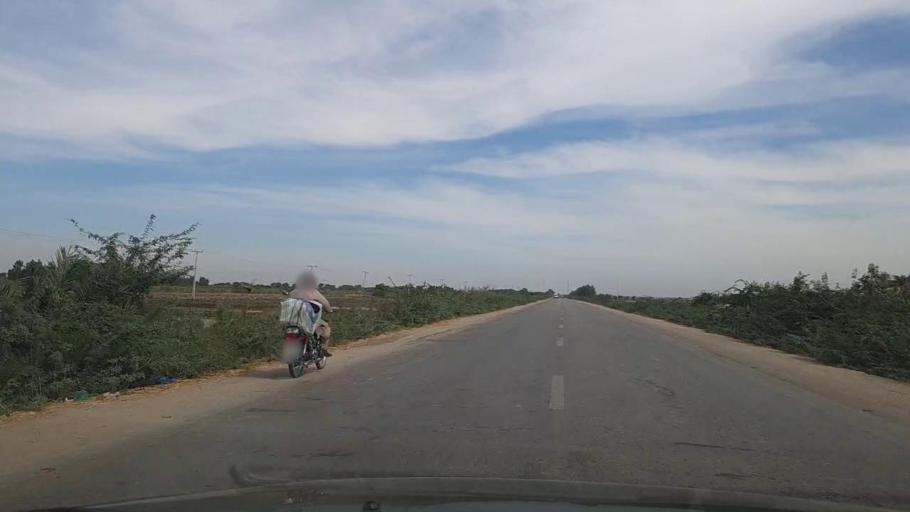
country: PK
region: Sindh
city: Thatta
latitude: 24.7968
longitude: 67.9615
